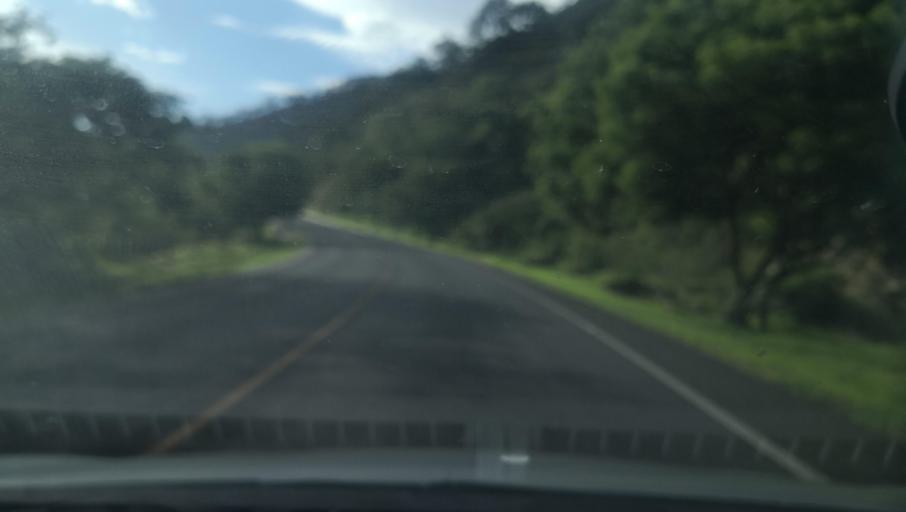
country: NI
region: Nueva Segovia
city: Mozonte
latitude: 13.7051
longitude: -86.4947
